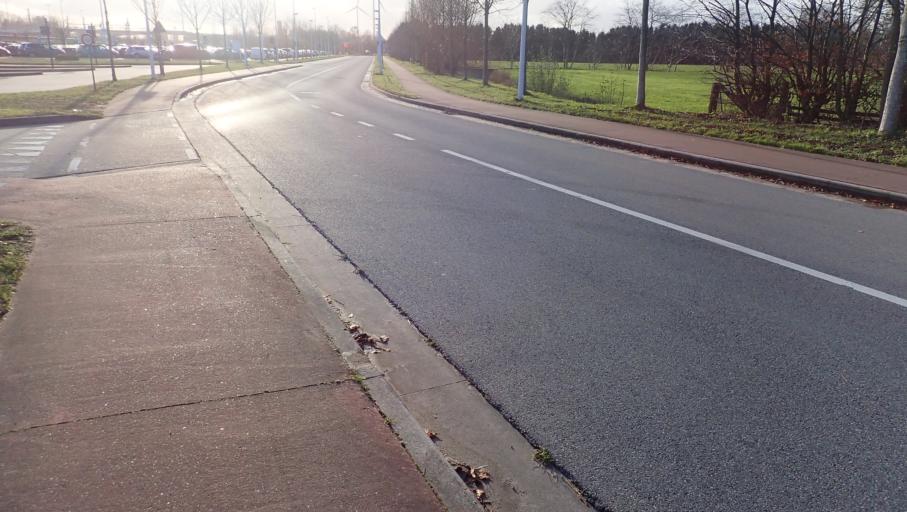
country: BE
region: Flanders
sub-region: Provincie Antwerpen
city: Brecht
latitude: 51.3579
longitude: 4.6324
